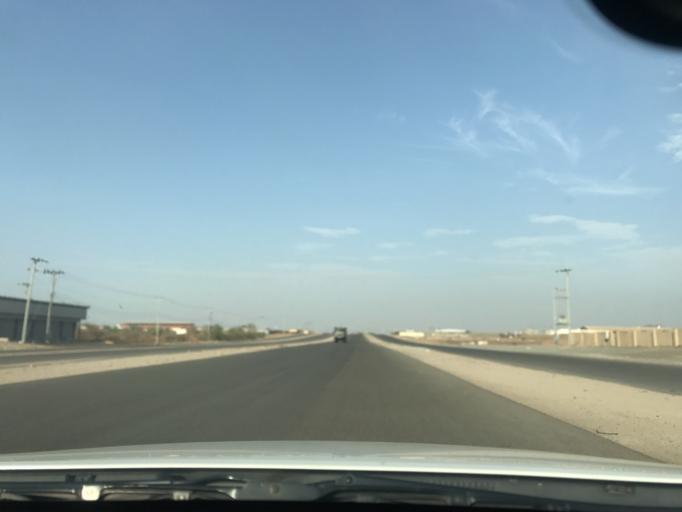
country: SA
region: Makkah
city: Al Jumum
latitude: 21.4524
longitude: 39.5295
